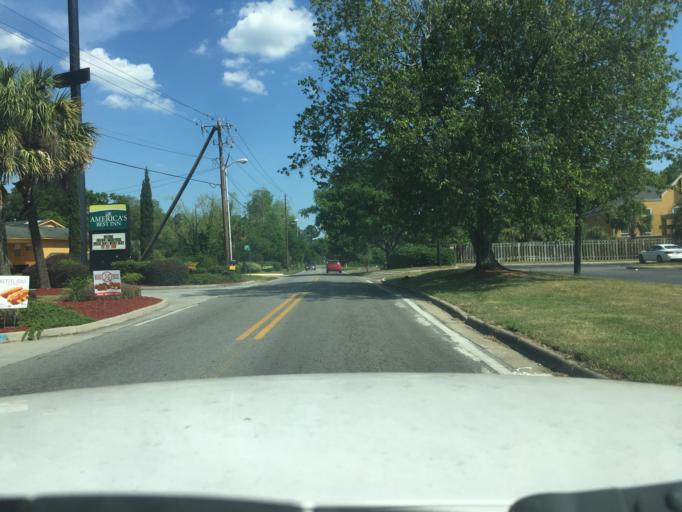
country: US
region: Georgia
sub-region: Chatham County
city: Georgetown
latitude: 32.0029
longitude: -81.2812
